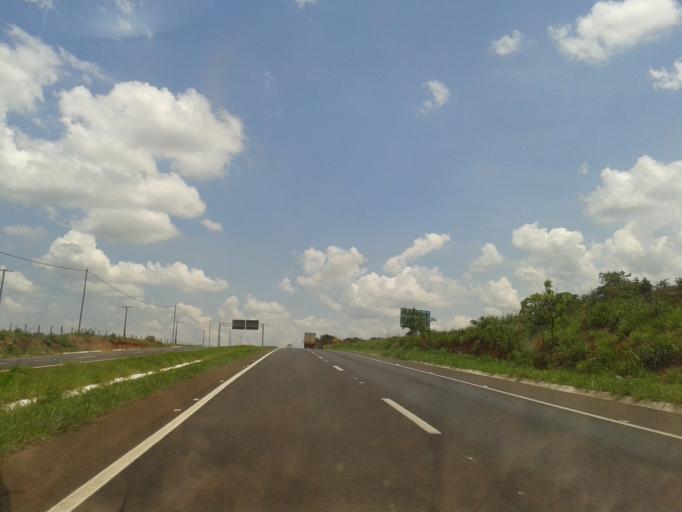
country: BR
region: Minas Gerais
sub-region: Uberlandia
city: Uberlandia
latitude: -18.8868
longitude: -48.4564
